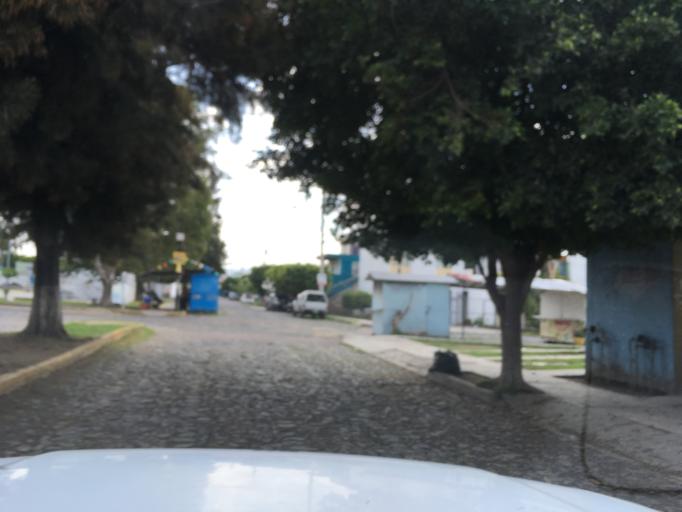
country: MX
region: Jalisco
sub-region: Tlajomulco de Zuniga
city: Altus Bosques
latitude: 20.5780
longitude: -103.3831
